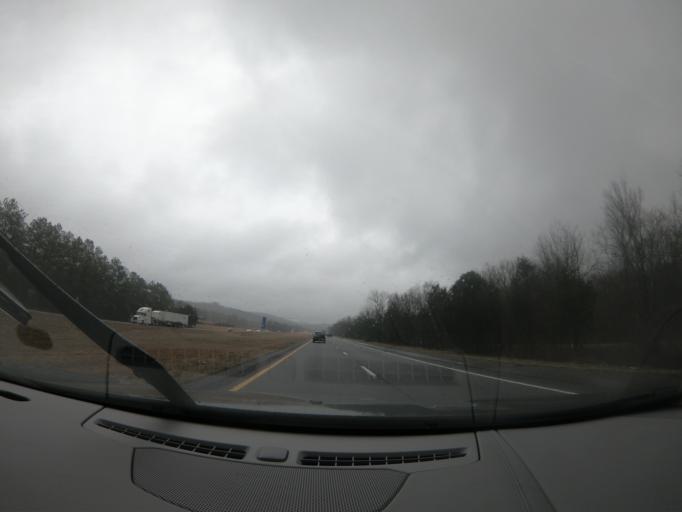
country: US
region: Tennessee
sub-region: Rutherford County
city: Plainview
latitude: 35.6560
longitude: -86.2643
